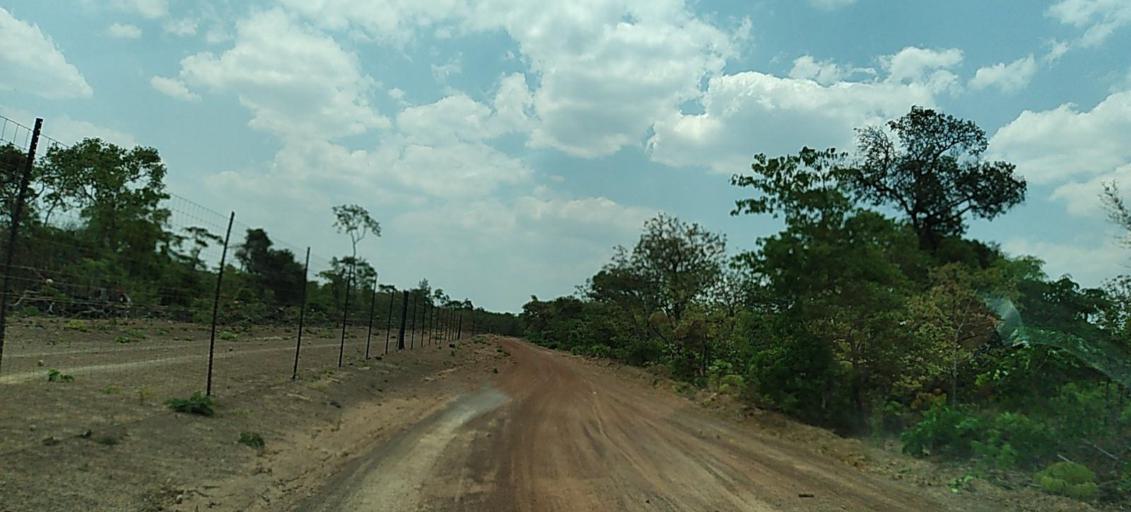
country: ZM
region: Copperbelt
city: Chililabombwe
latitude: -12.5247
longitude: 27.6260
